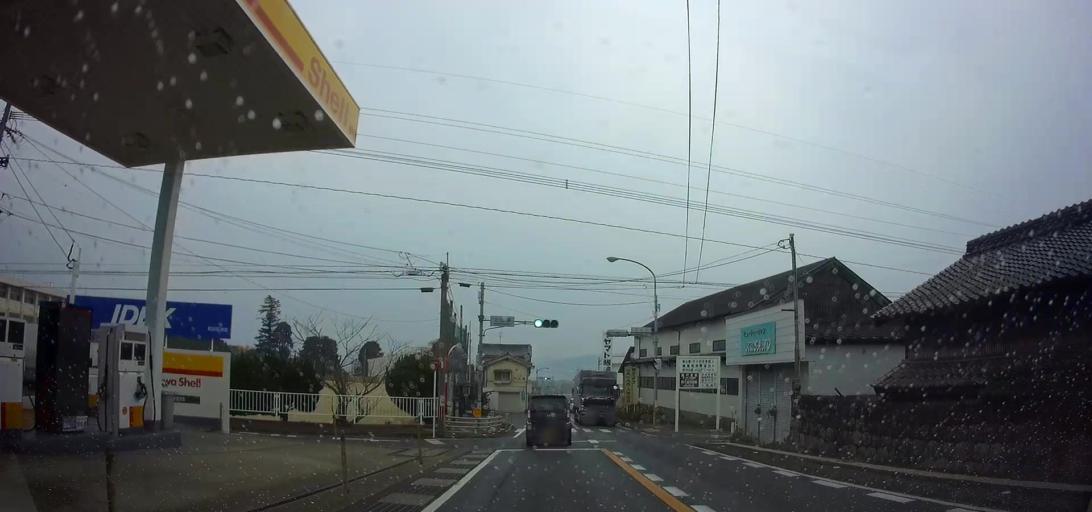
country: JP
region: Nagasaki
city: Shimabara
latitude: 32.7850
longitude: 130.2012
